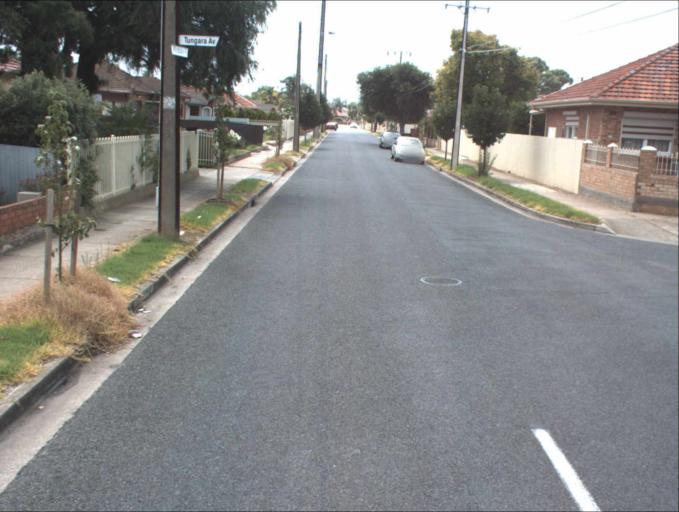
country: AU
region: South Australia
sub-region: Charles Sturt
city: Woodville
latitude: -34.8802
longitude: 138.5635
